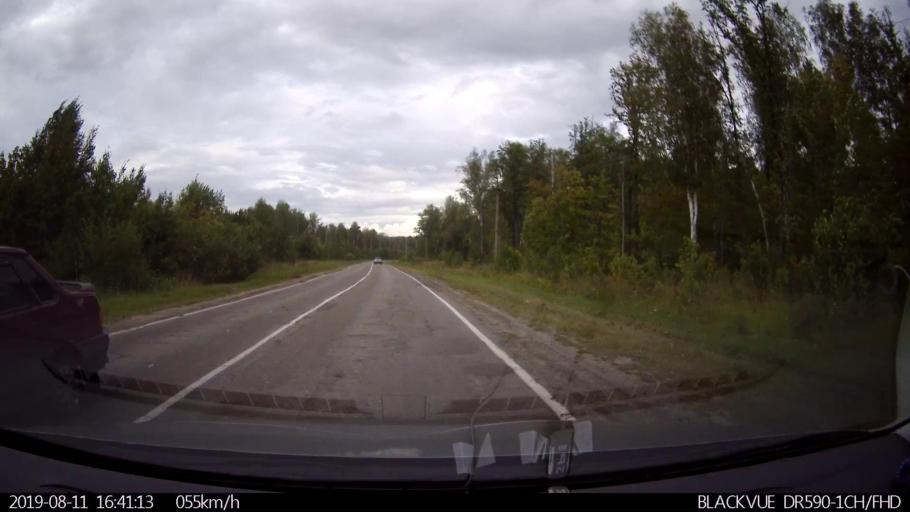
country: RU
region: Ulyanovsk
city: Mayna
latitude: 54.1516
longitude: 47.6513
